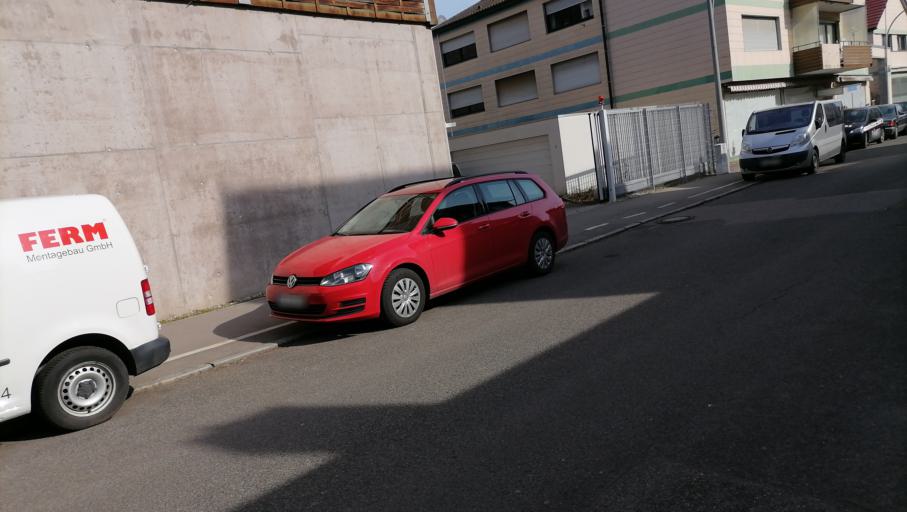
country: DE
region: Baden-Wuerttemberg
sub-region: Regierungsbezirk Stuttgart
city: Fellbach
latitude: 48.8178
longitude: 9.2676
